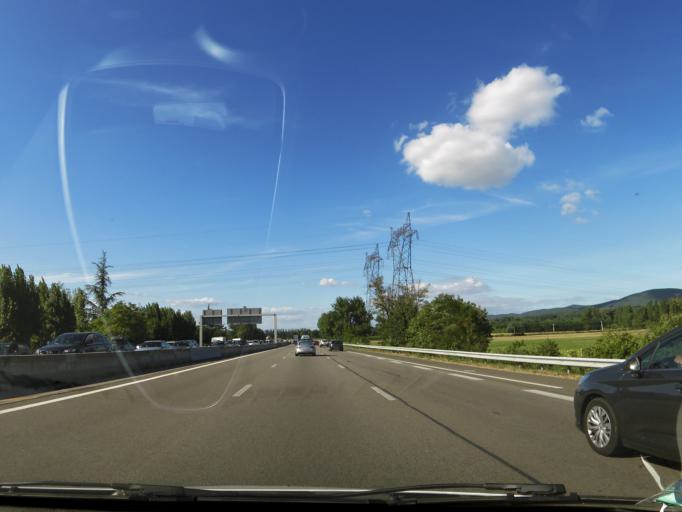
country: FR
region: Rhone-Alpes
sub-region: Departement de la Drome
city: Saulce-sur-Rhone
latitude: 44.6733
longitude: 4.7976
